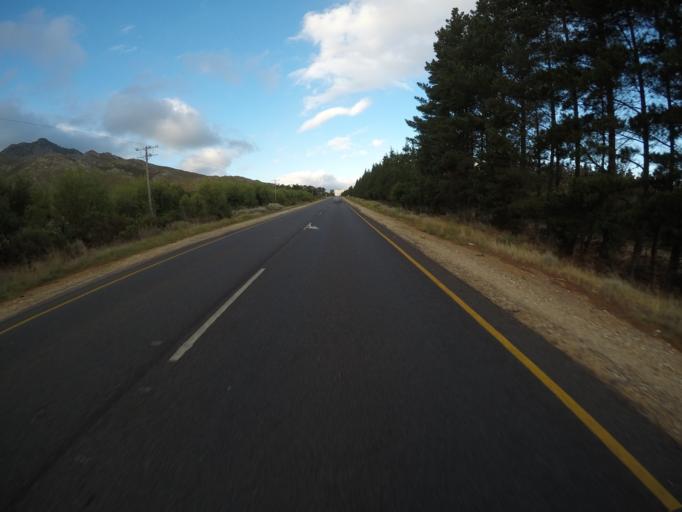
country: ZA
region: Western Cape
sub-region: Overberg District Municipality
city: Grabouw
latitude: -34.0210
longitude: 19.2282
